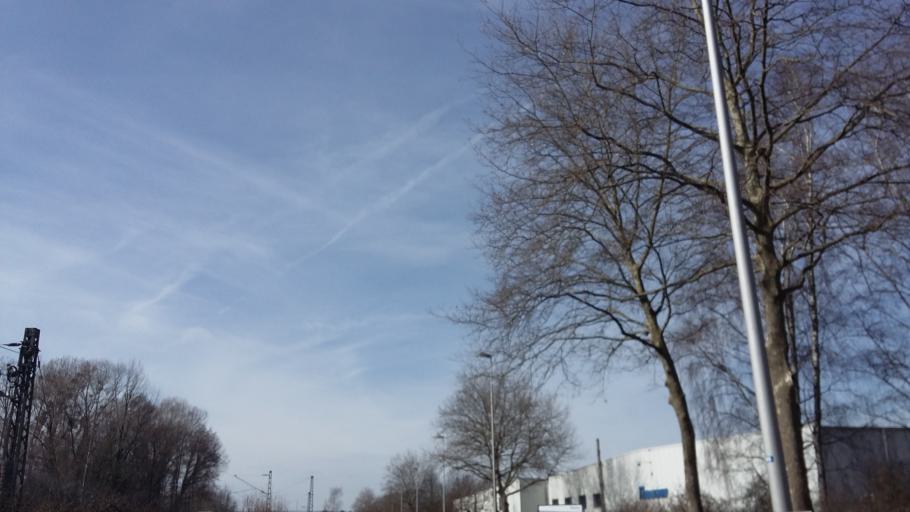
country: AT
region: Vorarlberg
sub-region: Politischer Bezirk Bregenz
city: Horbranz
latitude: 47.5515
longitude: 9.7174
